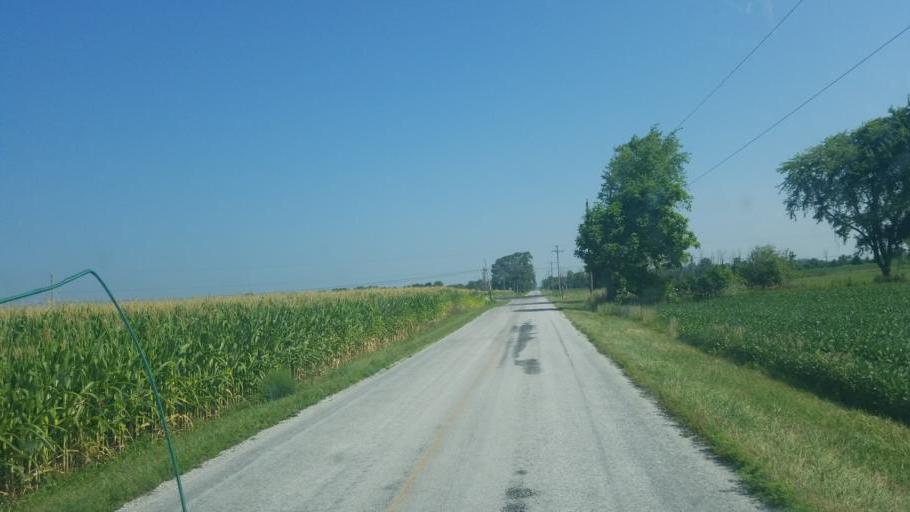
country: US
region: Ohio
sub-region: Hardin County
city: Kenton
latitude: 40.6698
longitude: -83.5380
